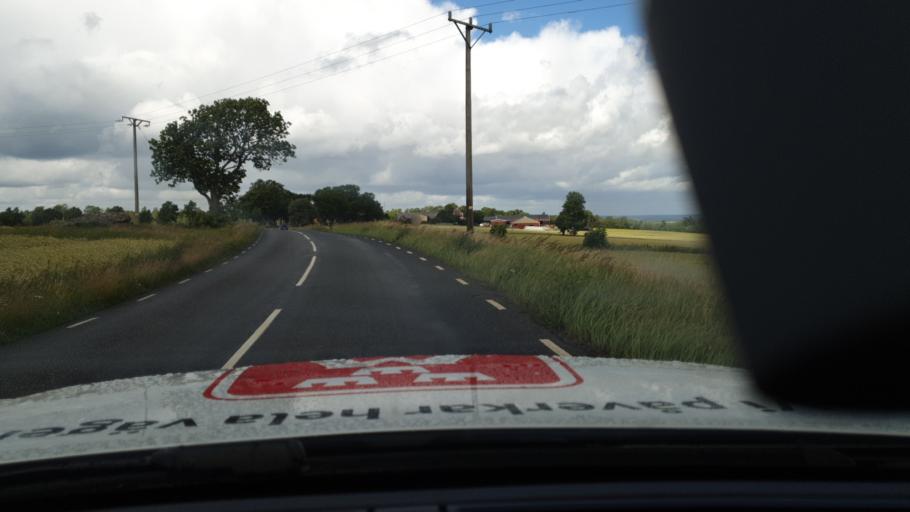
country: SE
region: Vaestra Goetaland
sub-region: Falkopings Kommun
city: Akarp
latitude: 58.1657
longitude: 13.6373
